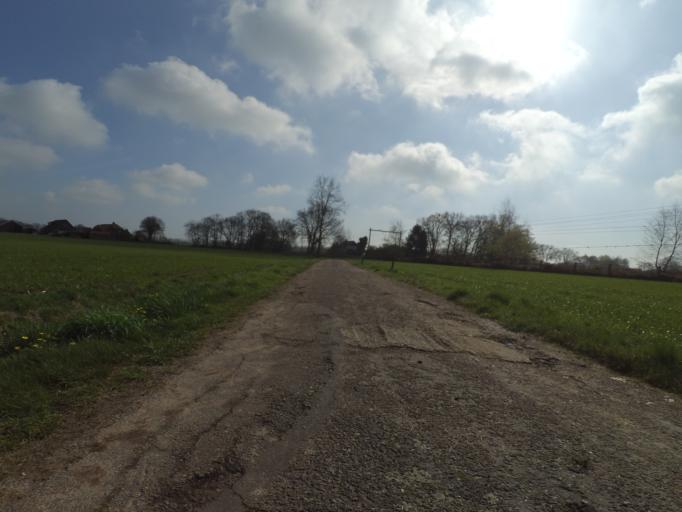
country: NL
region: Gelderland
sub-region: Gemeente Barneveld
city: Terschuur
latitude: 52.1629
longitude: 5.5544
